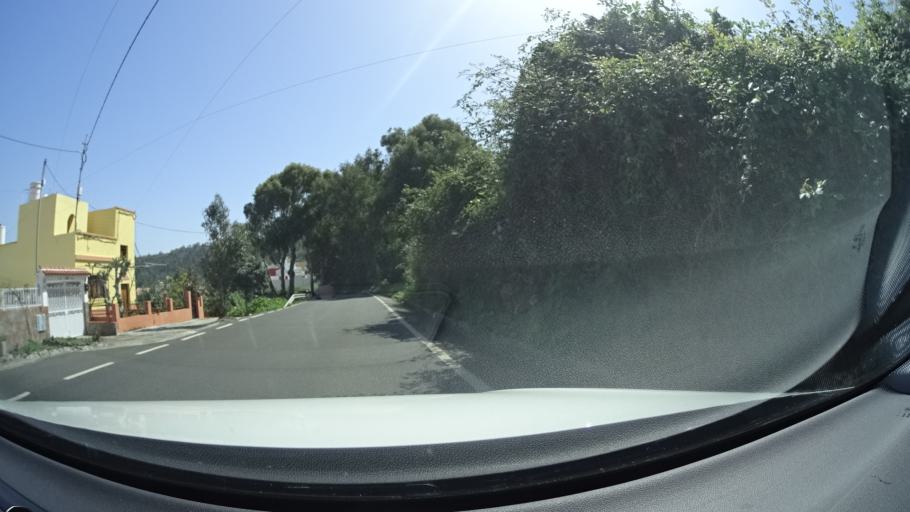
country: ES
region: Canary Islands
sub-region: Provincia de Las Palmas
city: Arucas
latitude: 28.0974
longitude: -15.5363
